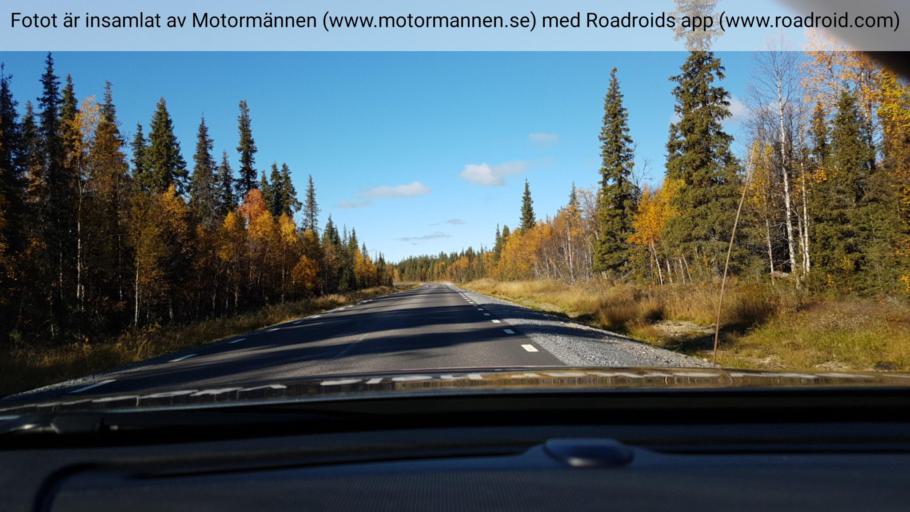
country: SE
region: Norrbotten
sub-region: Gallivare Kommun
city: Gaellivare
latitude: 66.9332
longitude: 20.8663
